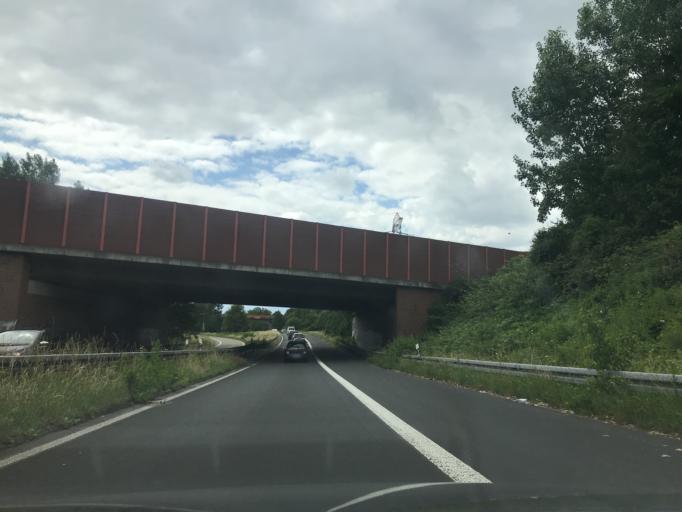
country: DE
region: North Rhine-Westphalia
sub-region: Regierungsbezirk Dusseldorf
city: Ratingen
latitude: 51.2812
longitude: 6.8089
